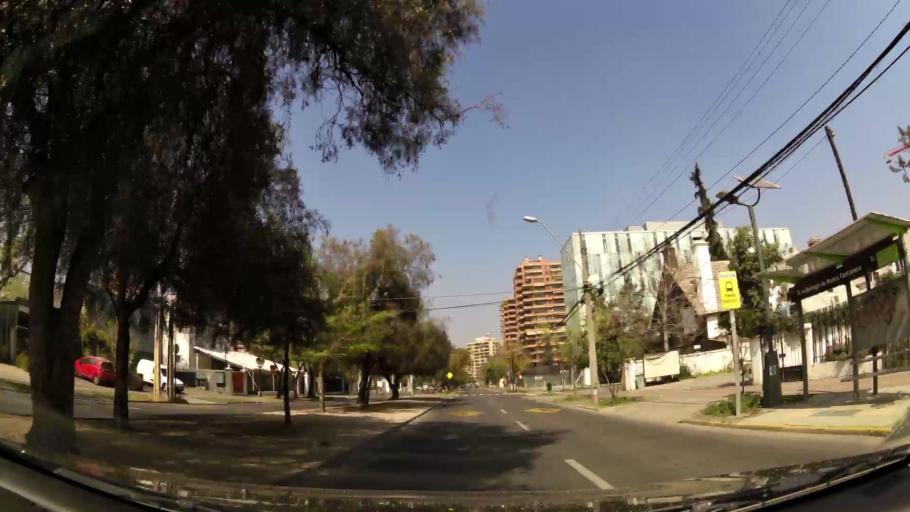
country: CL
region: Santiago Metropolitan
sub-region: Provincia de Santiago
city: Villa Presidente Frei, Nunoa, Santiago, Chile
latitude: -33.4041
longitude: -70.5987
